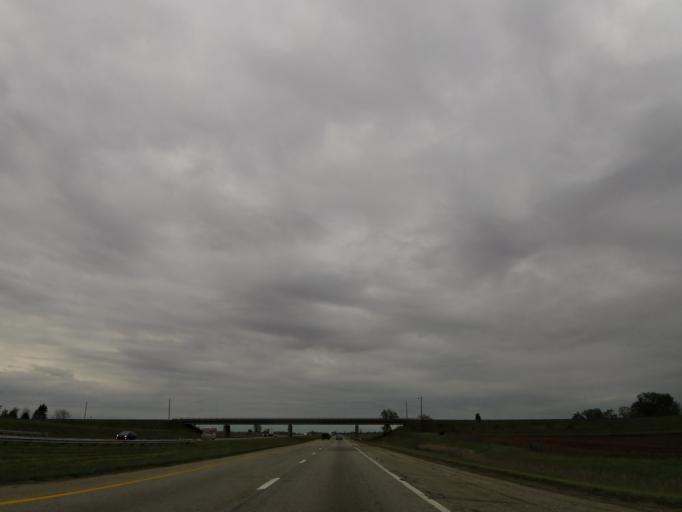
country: US
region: Ohio
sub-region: Madison County
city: Bethel
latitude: 39.7337
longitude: -83.3602
